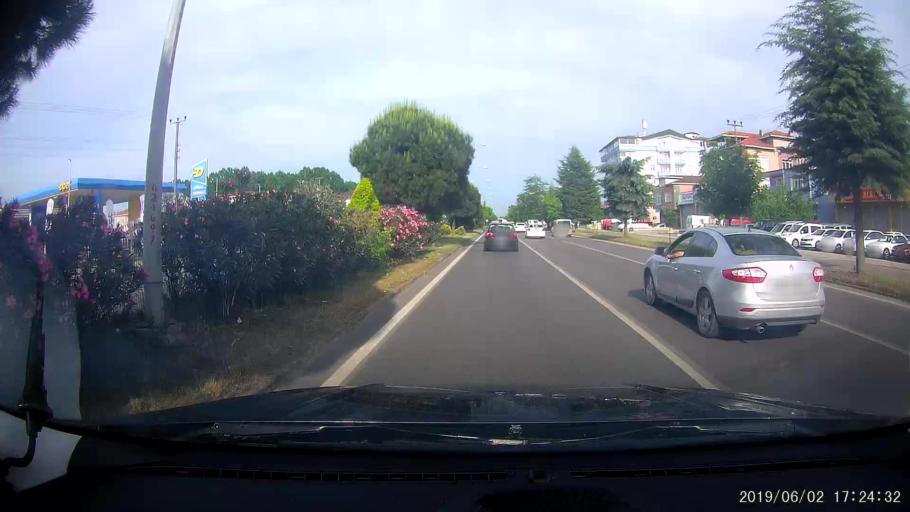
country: TR
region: Samsun
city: Carsamba
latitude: 41.2055
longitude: 36.7032
